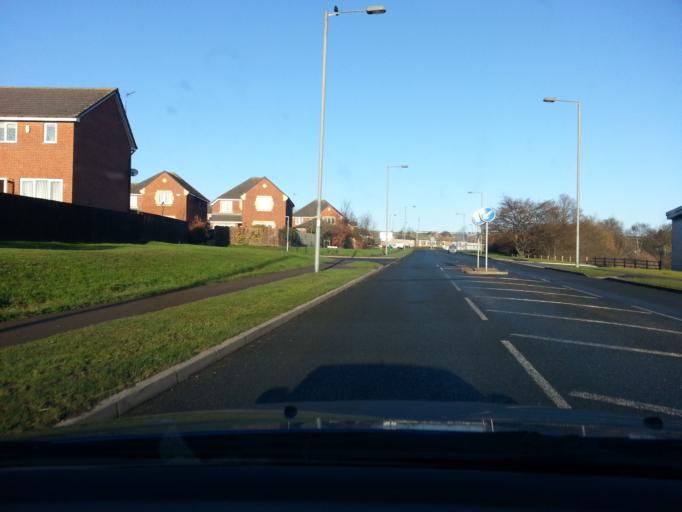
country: GB
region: England
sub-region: County Durham
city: Crook
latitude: 54.7111
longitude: -1.7518
